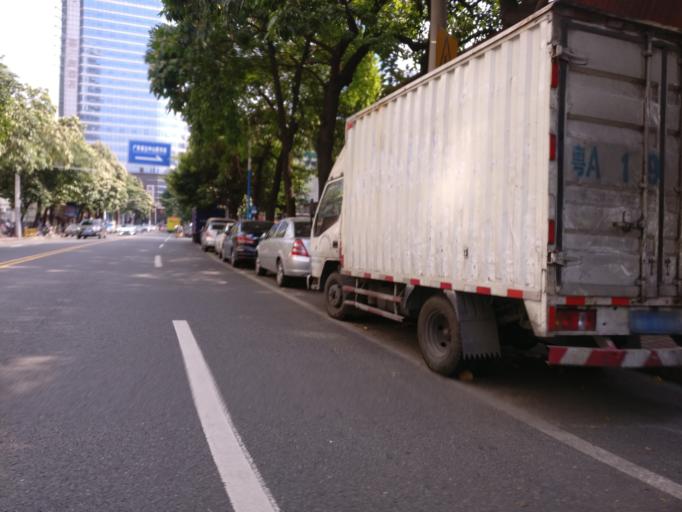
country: CN
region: Guangdong
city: Guangzhou
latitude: 23.1270
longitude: 113.2731
